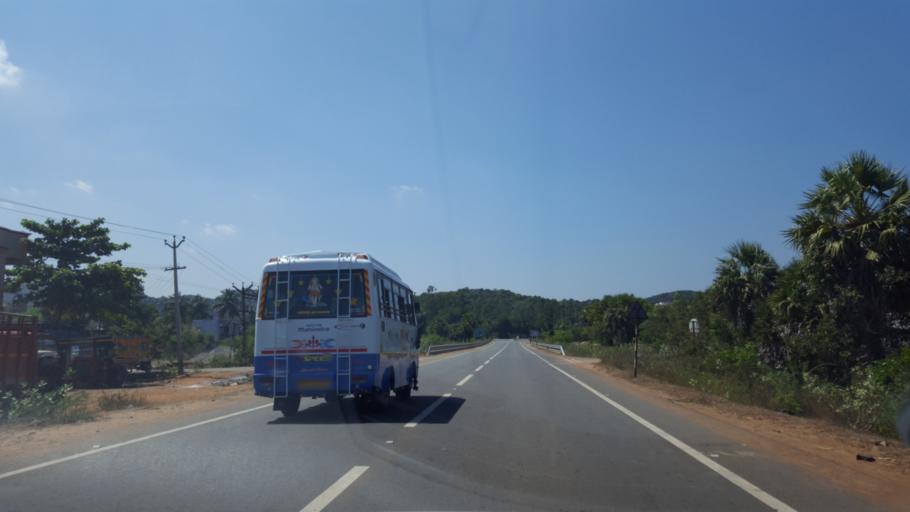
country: IN
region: Tamil Nadu
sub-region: Kancheepuram
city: Karumbakkam
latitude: 12.6244
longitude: 80.0553
